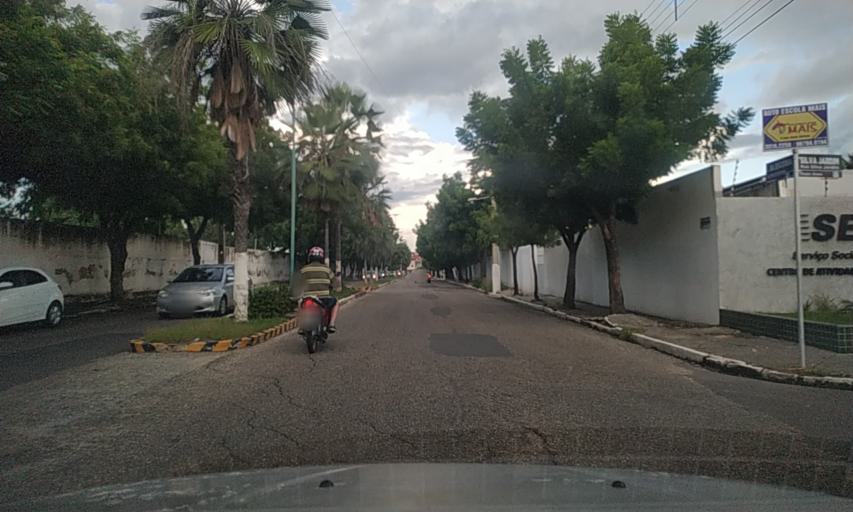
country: BR
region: Rio Grande do Norte
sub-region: Mossoro
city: Mossoro
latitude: -5.1890
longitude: -37.3491
